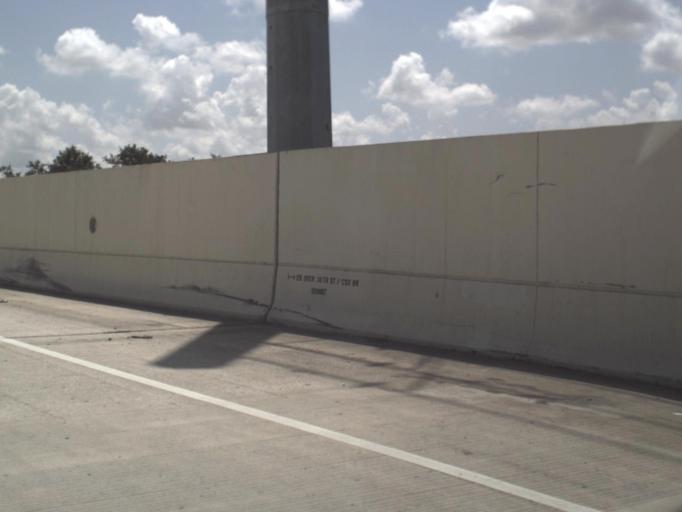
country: US
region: Florida
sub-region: Hillsborough County
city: Tampa
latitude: 27.9646
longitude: -82.4197
